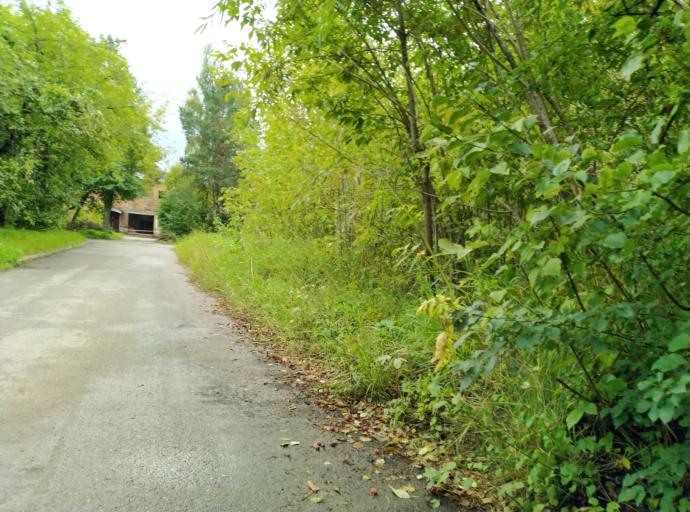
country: RU
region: Krasnoyarskiy
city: Krasnoyarsk
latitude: 55.9889
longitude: 92.7616
